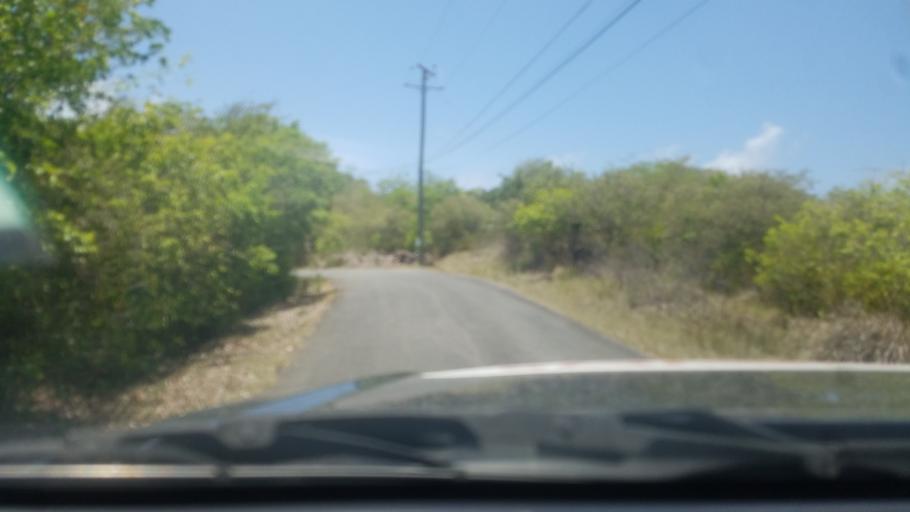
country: LC
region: Vieux-Fort
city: Vieux Fort
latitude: 13.7144
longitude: -60.9475
